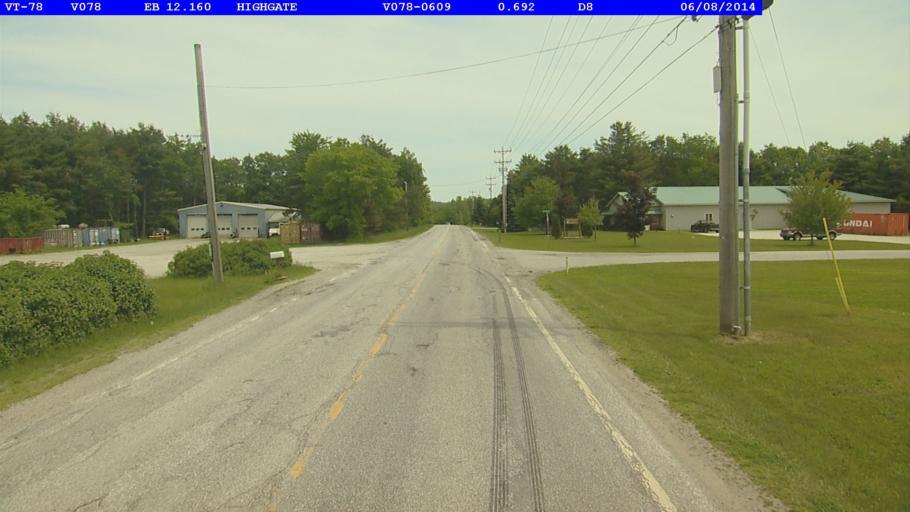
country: US
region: Vermont
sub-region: Franklin County
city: Swanton
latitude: 44.9317
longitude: -73.0869
